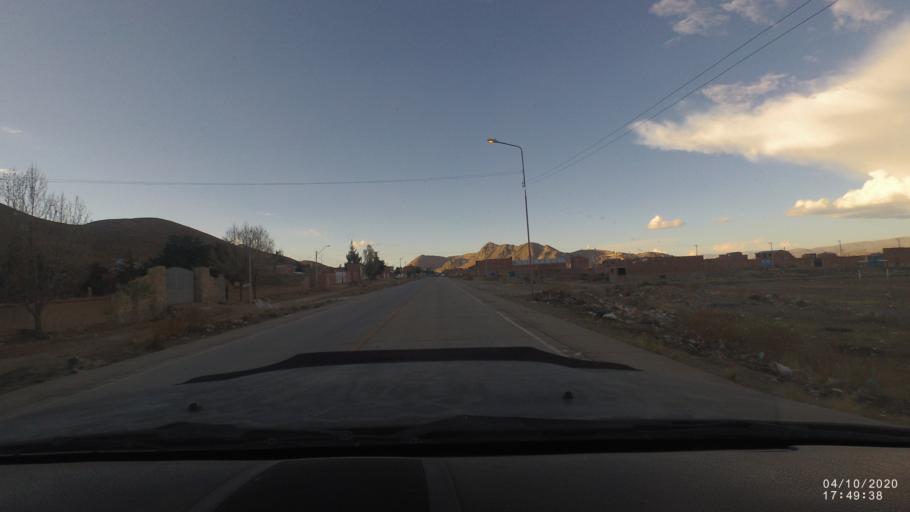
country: BO
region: Oruro
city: Oruro
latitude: -18.0090
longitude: -67.1365
